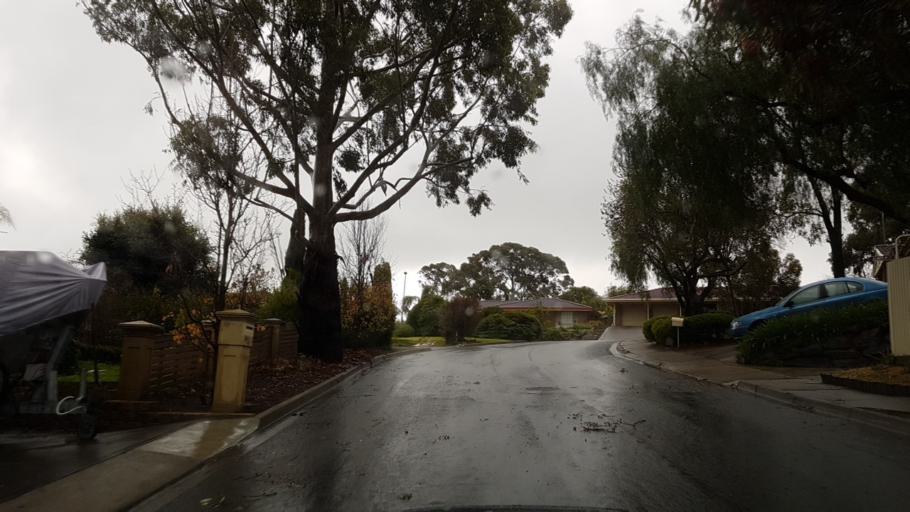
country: AU
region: South Australia
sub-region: Marion
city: Trott Park
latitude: -35.0932
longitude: 138.5881
